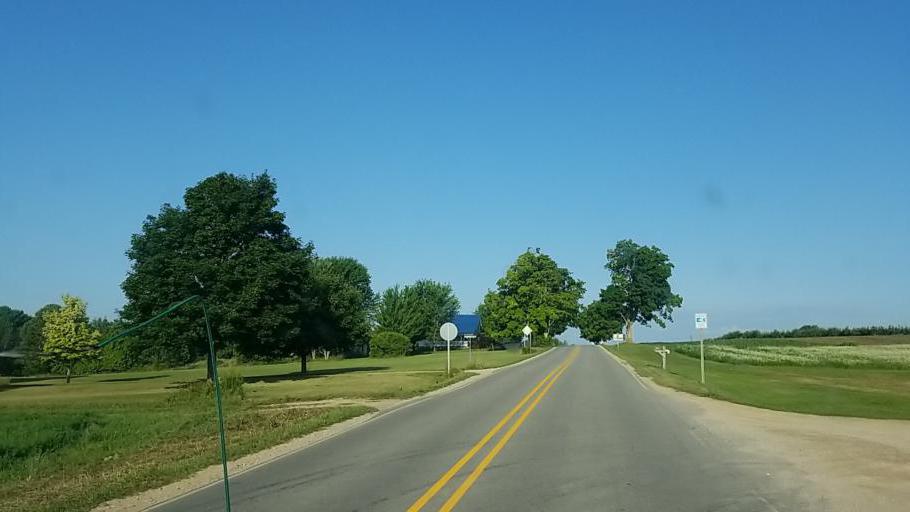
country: US
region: Michigan
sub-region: Newaygo County
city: Newaygo
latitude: 43.3512
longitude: -85.8129
